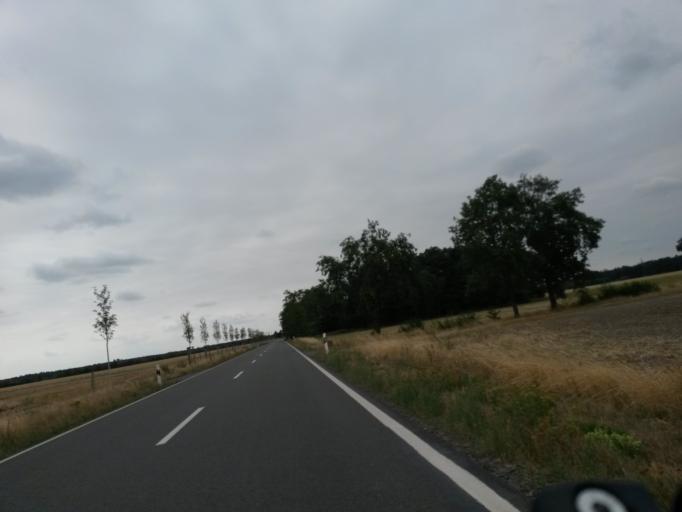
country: DE
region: Saxony-Anhalt
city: Zahna
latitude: 51.8737
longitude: 12.7870
